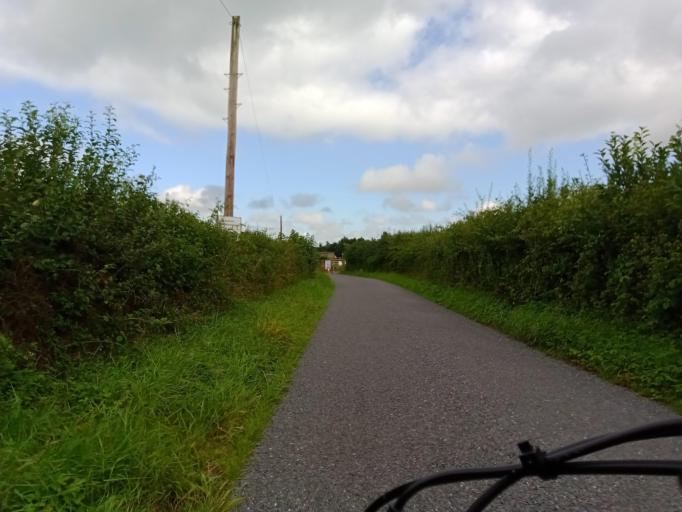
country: IE
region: Leinster
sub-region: Kilkenny
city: Callan
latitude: 52.5367
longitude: -7.2861
